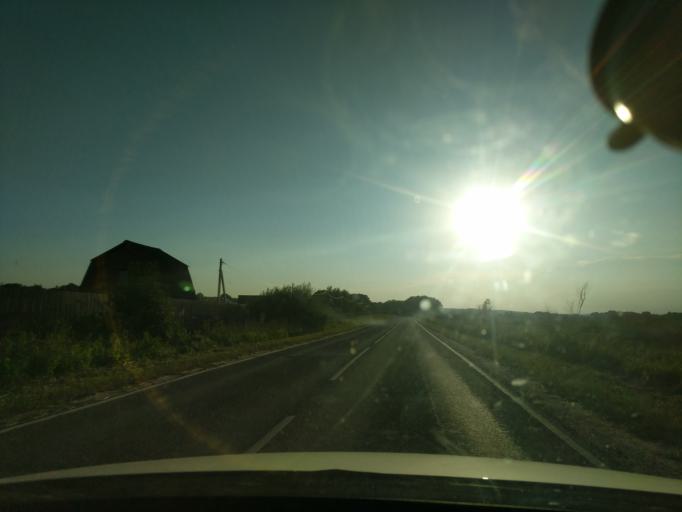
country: RU
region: Moskovskaya
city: Pushchino
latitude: 54.8437
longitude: 37.5361
